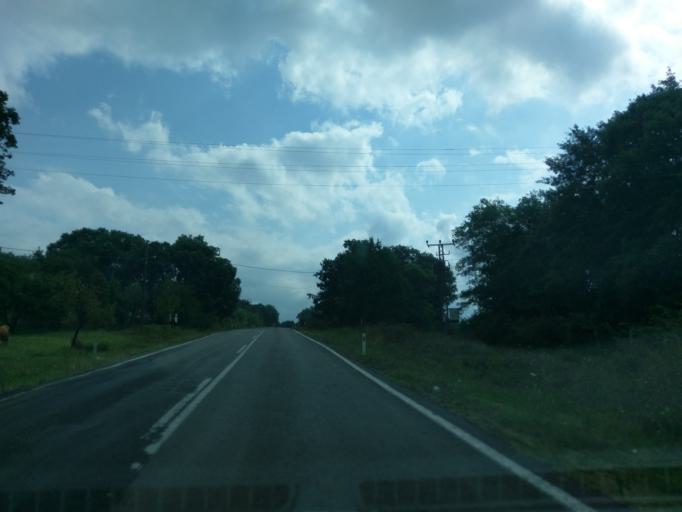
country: TR
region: Sinop
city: Erfelek
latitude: 41.9464
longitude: 34.7915
